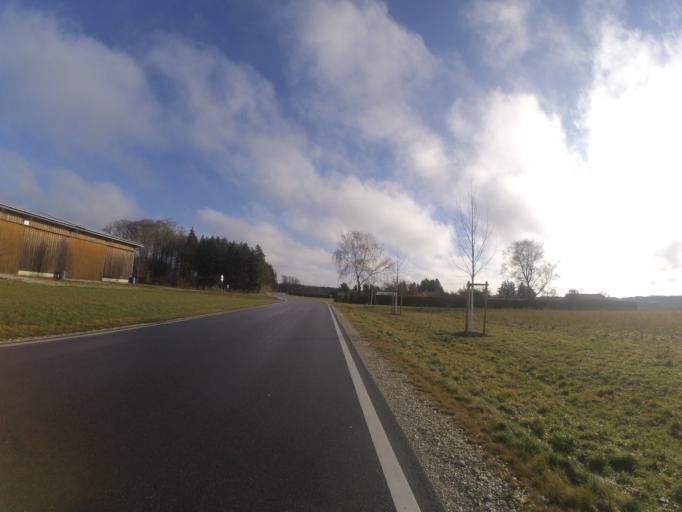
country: DE
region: Baden-Wuerttemberg
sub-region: Tuebingen Region
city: Ulm
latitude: 48.4414
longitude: 10.0012
